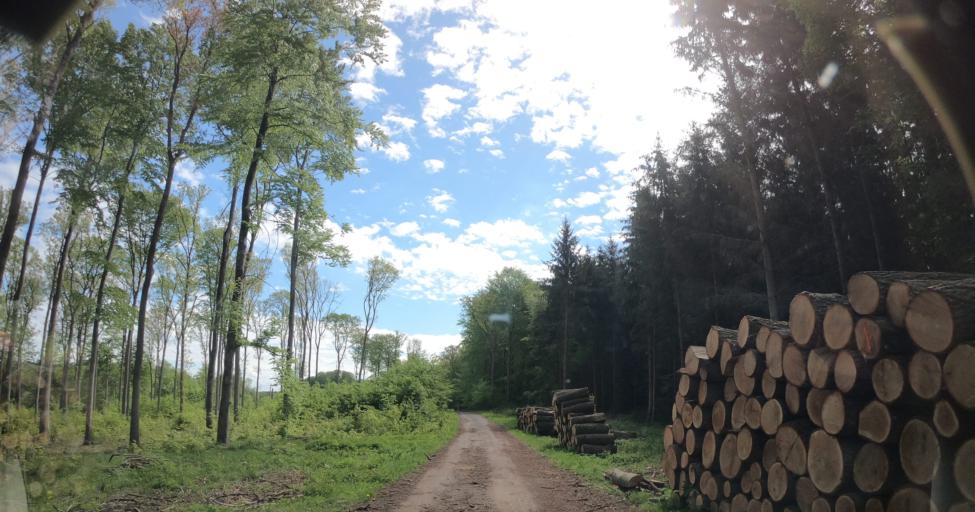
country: PL
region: West Pomeranian Voivodeship
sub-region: Powiat stargardzki
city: Dobrzany
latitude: 53.3477
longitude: 15.4889
